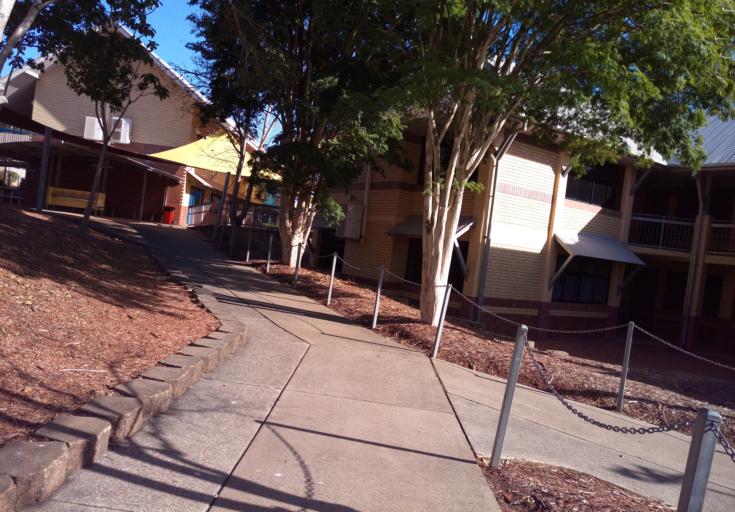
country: AU
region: Queensland
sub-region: Ipswich
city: Brassall
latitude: -27.5871
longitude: 152.7050
